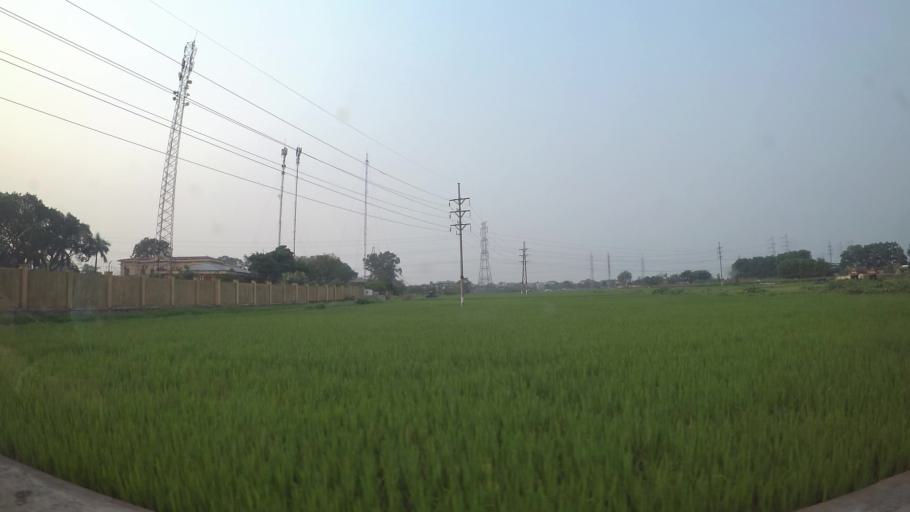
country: VN
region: Ha Noi
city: Thuong Tin
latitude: 20.8784
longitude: 105.8656
